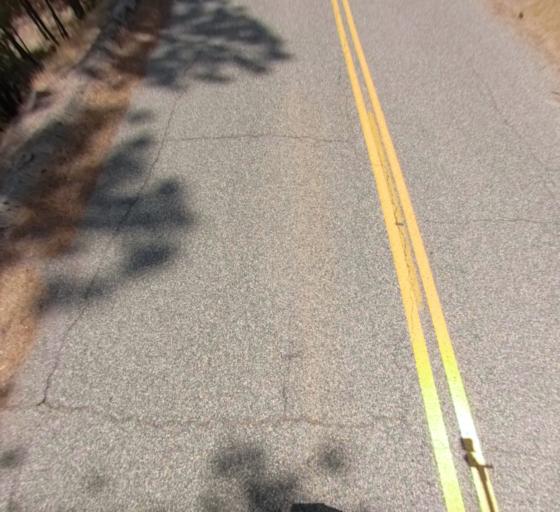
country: US
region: California
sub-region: Madera County
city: Oakhurst
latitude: 37.3834
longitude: -119.3574
